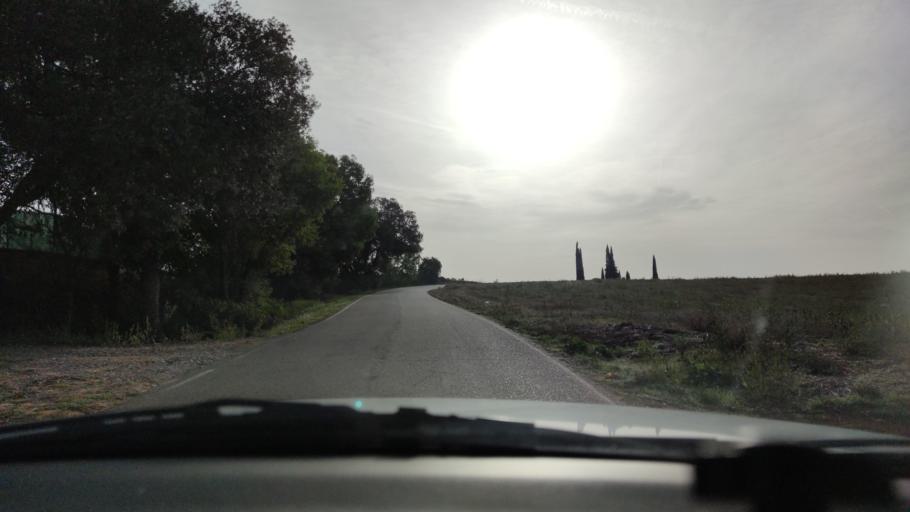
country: ES
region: Catalonia
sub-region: Provincia de Lleida
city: Artesa de Segre
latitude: 41.9177
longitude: 1.0201
